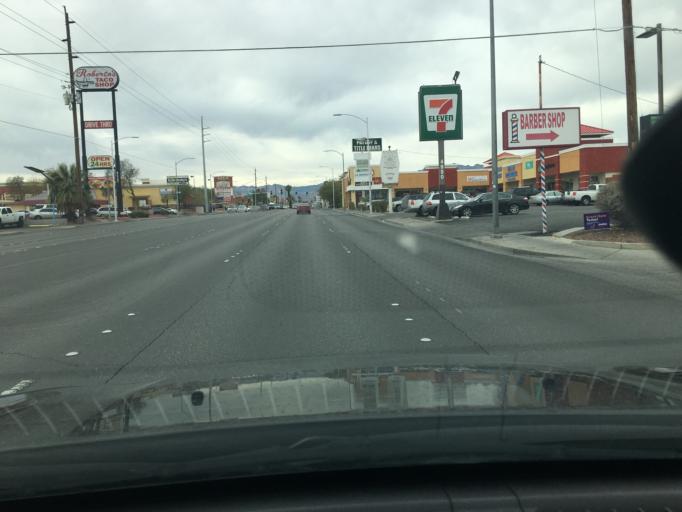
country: US
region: Nevada
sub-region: Clark County
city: Spring Valley
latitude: 36.1592
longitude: -115.2079
